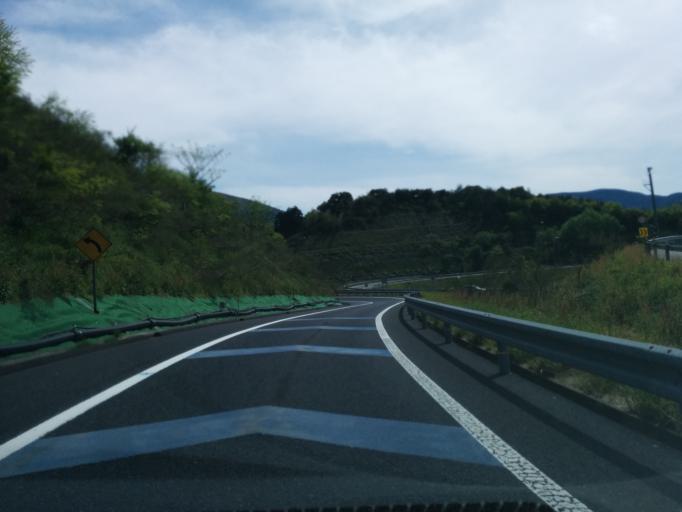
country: JP
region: Kyoto
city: Miyazu
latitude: 35.5150
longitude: 135.1939
